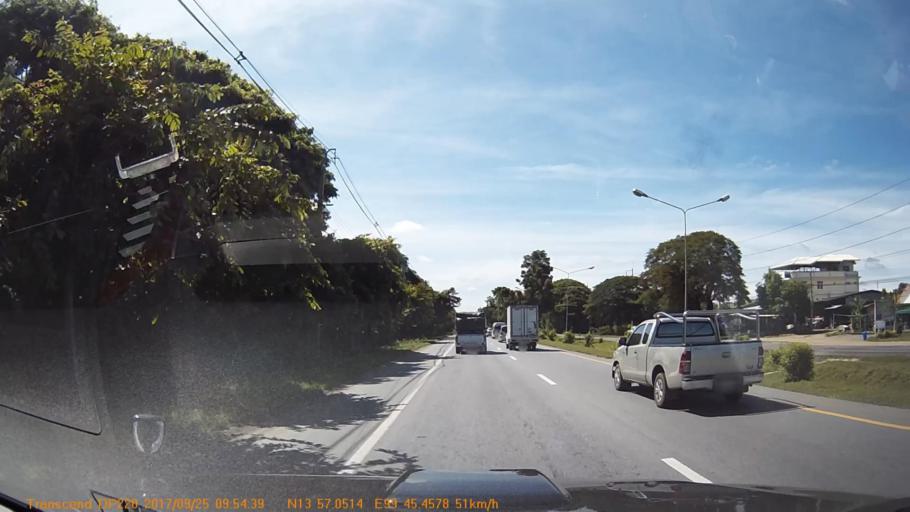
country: TH
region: Kanchanaburi
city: Tha Maka
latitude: 13.9505
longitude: 99.7578
